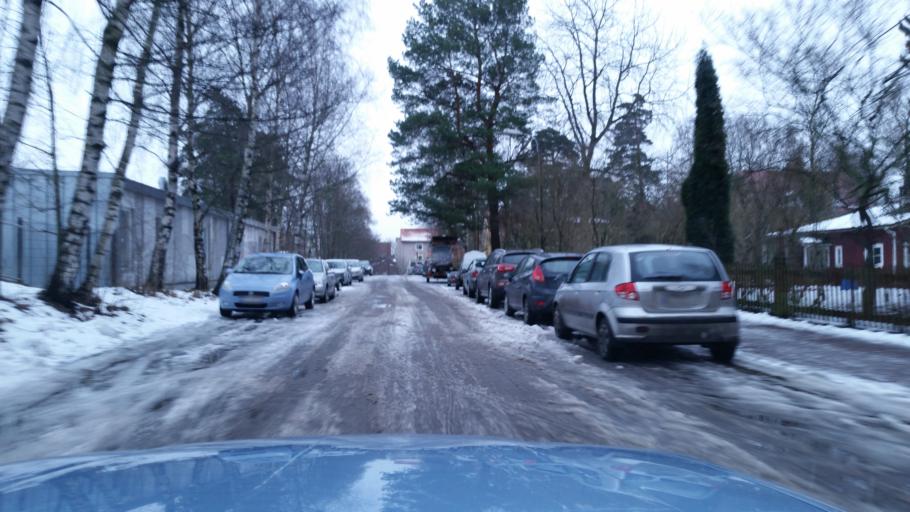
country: FI
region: Uusimaa
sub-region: Helsinki
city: Helsinki
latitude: 60.2085
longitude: 24.9705
